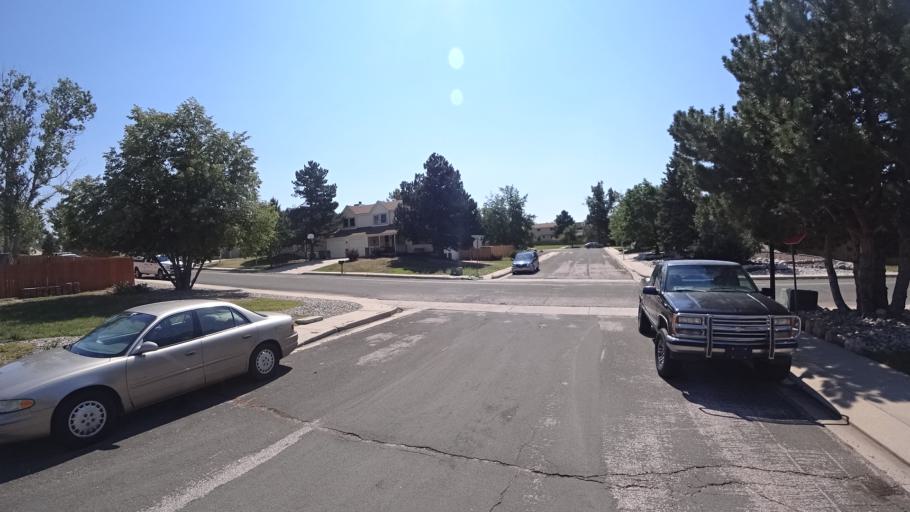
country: US
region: Colorado
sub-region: El Paso County
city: Air Force Academy
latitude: 38.9572
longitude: -104.7777
